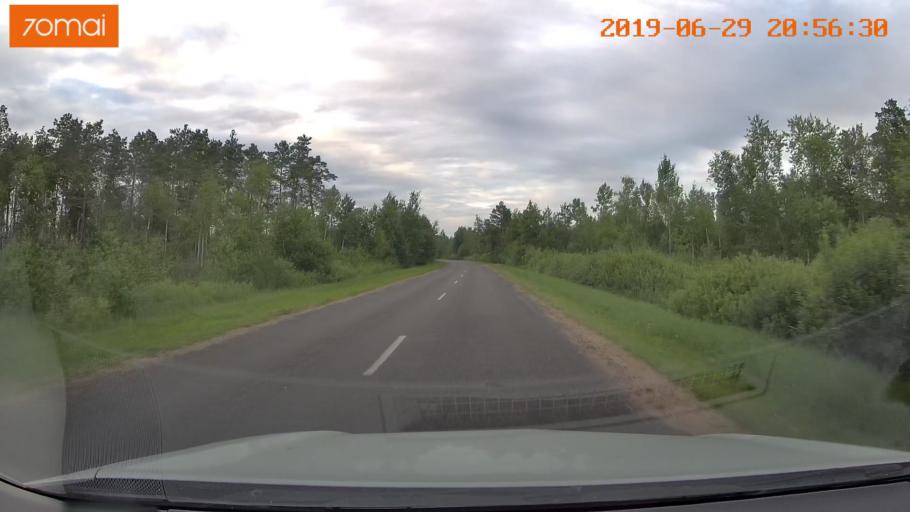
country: BY
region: Brest
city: Hantsavichy
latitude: 52.7062
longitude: 26.3680
